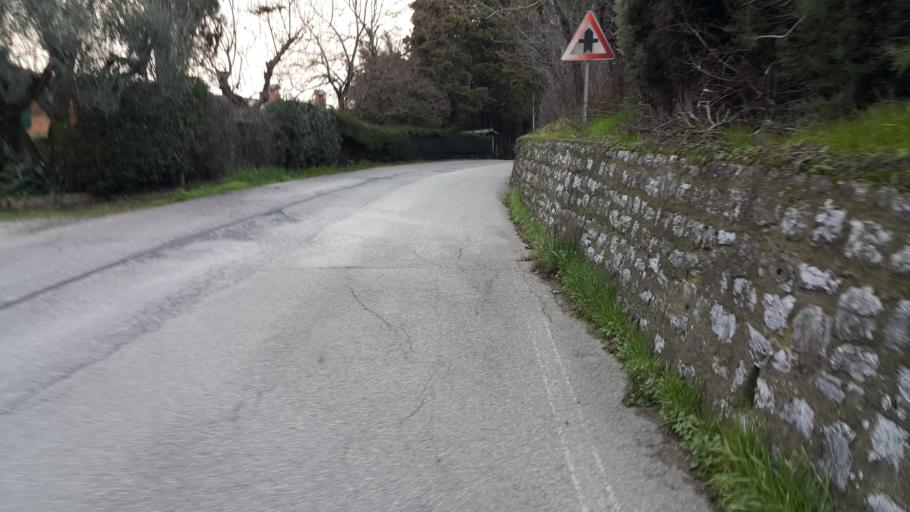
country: IT
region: Umbria
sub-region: Provincia di Perugia
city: Perugia
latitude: 43.0914
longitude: 12.3757
